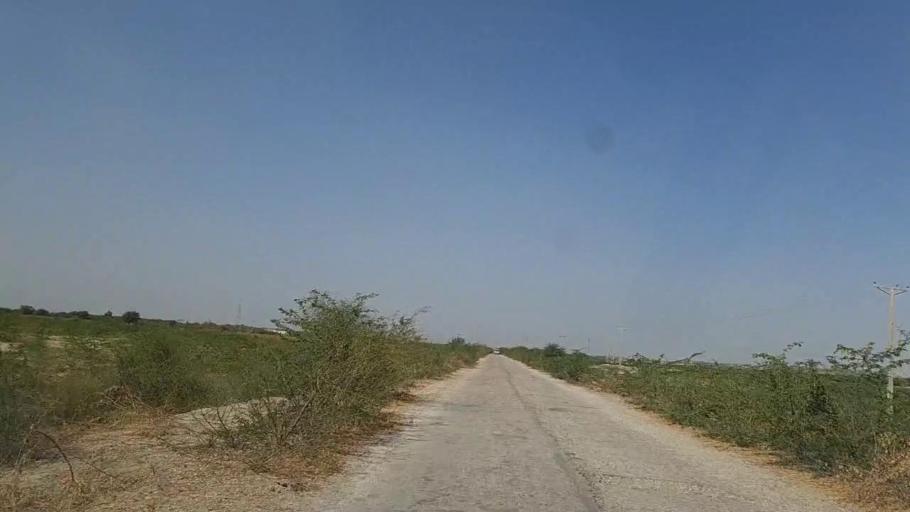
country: PK
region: Sindh
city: Naukot
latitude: 24.6442
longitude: 69.2879
